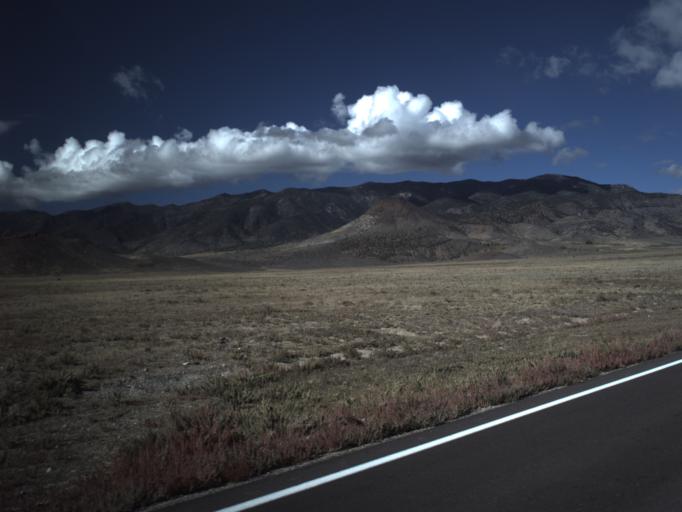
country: US
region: Utah
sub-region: Beaver County
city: Milford
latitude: 38.4820
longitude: -113.4423
